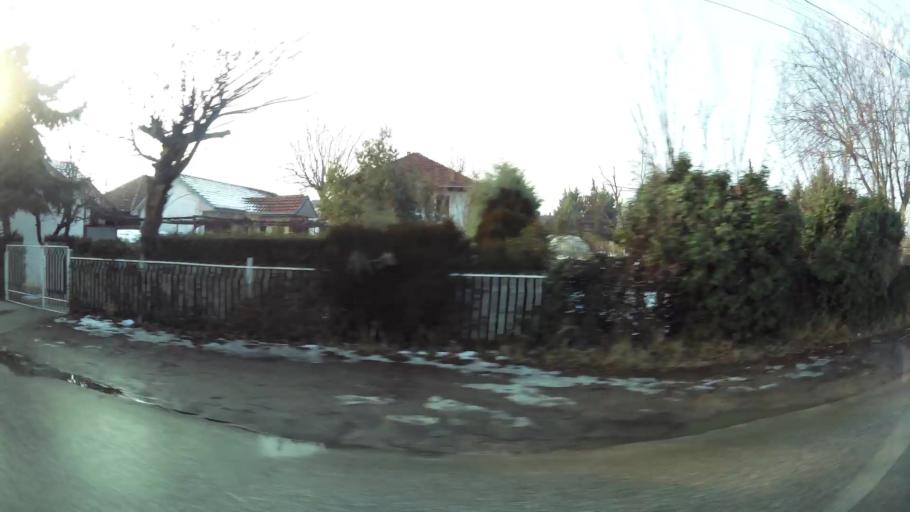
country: MK
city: Miladinovci
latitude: 41.9874
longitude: 21.6519
